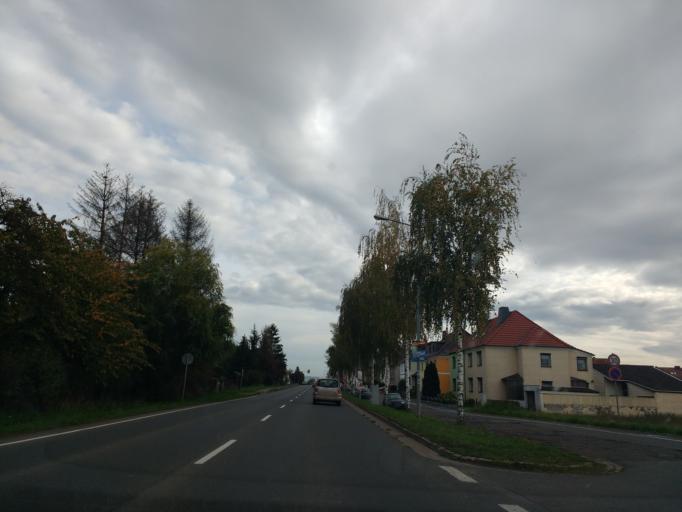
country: DE
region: Thuringia
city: Uthleben
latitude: 51.4868
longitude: 10.8382
